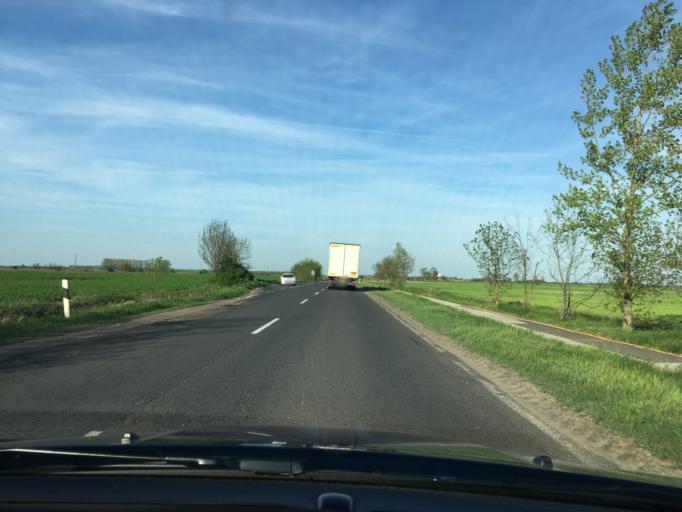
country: HU
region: Bekes
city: Korosladany
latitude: 46.9960
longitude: 21.0950
